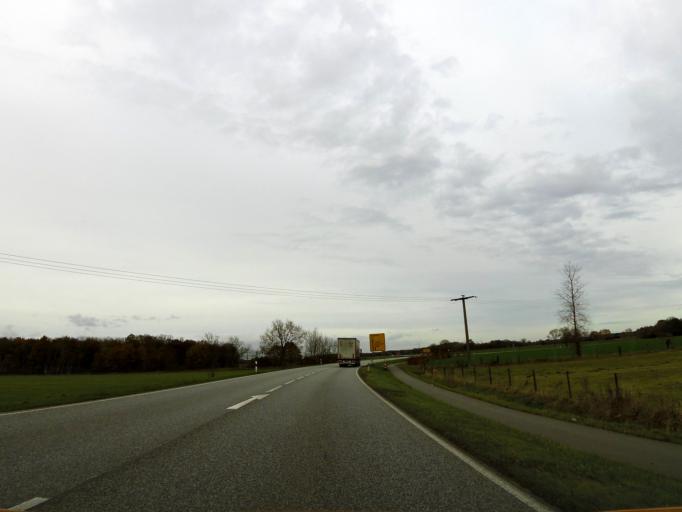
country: DE
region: Saxony-Anhalt
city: Pretzier
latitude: 52.7973
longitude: 11.2294
